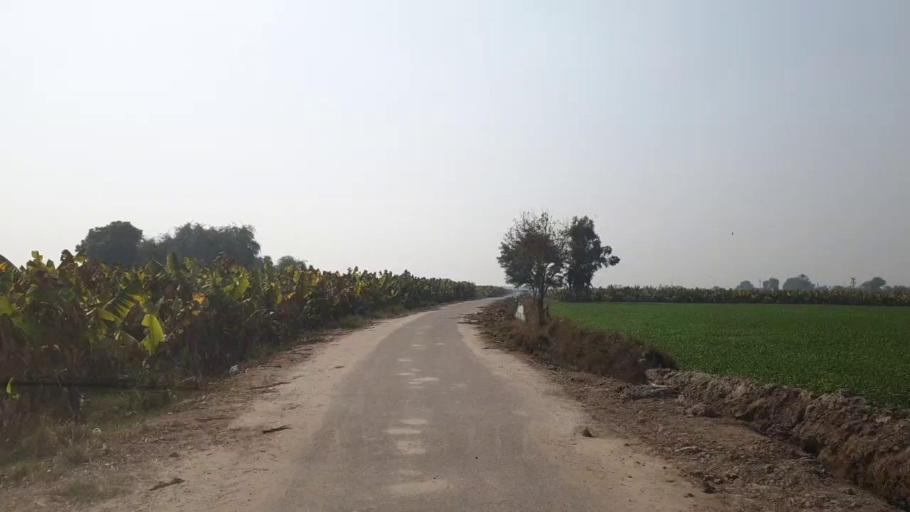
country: PK
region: Sindh
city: Bhit Shah
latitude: 25.7840
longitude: 68.4879
